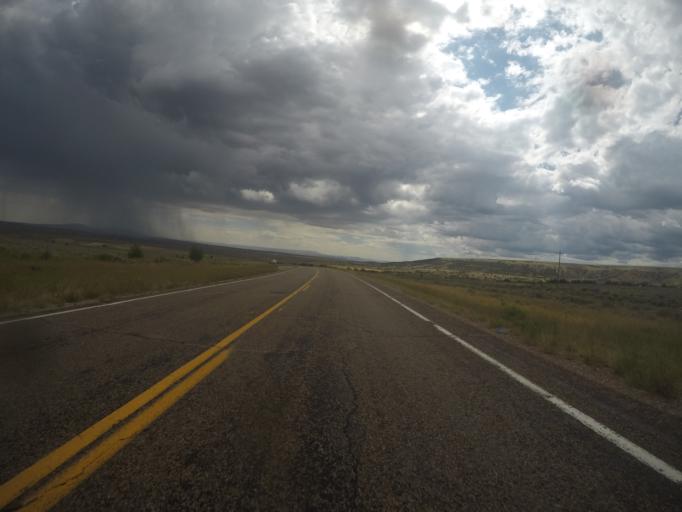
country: US
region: Utah
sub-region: Daggett County
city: Manila
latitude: 41.0218
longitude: -109.8977
